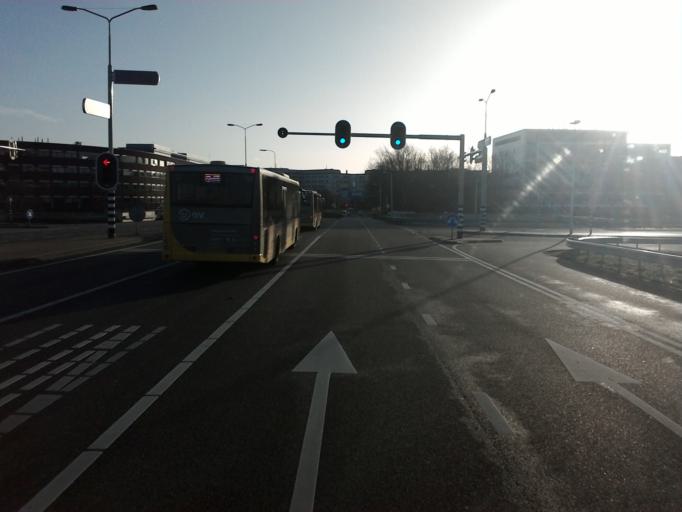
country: NL
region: Utrecht
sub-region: Gemeente De Bilt
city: De Bilt
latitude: 52.0915
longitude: 5.1796
